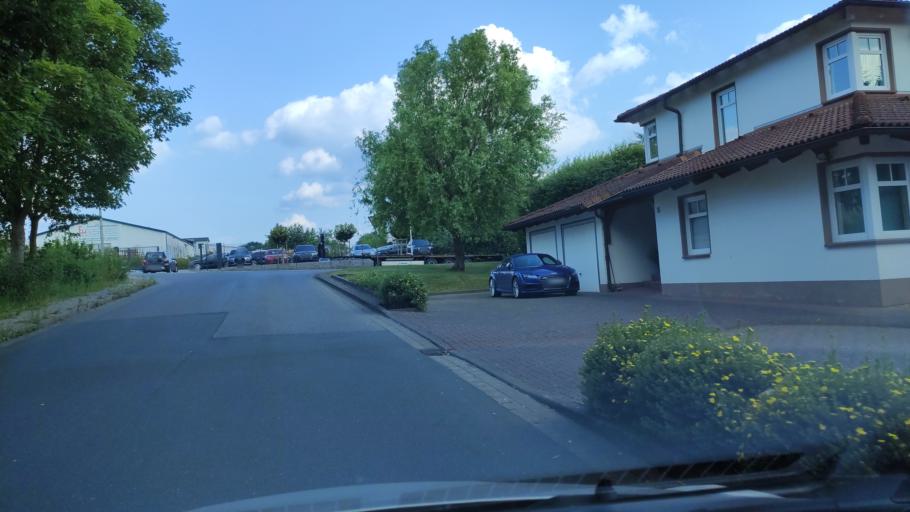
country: DE
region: Lower Saxony
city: Holzminden
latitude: 51.8408
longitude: 9.4616
